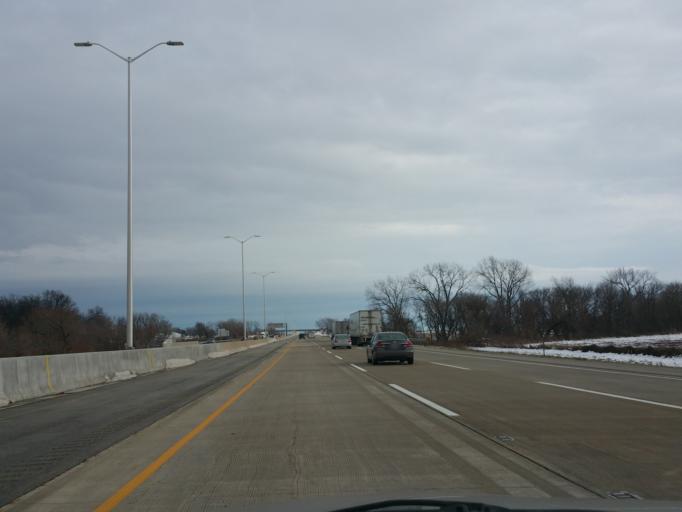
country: US
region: Illinois
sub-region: Boone County
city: Belvidere
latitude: 42.2296
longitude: -88.7751
